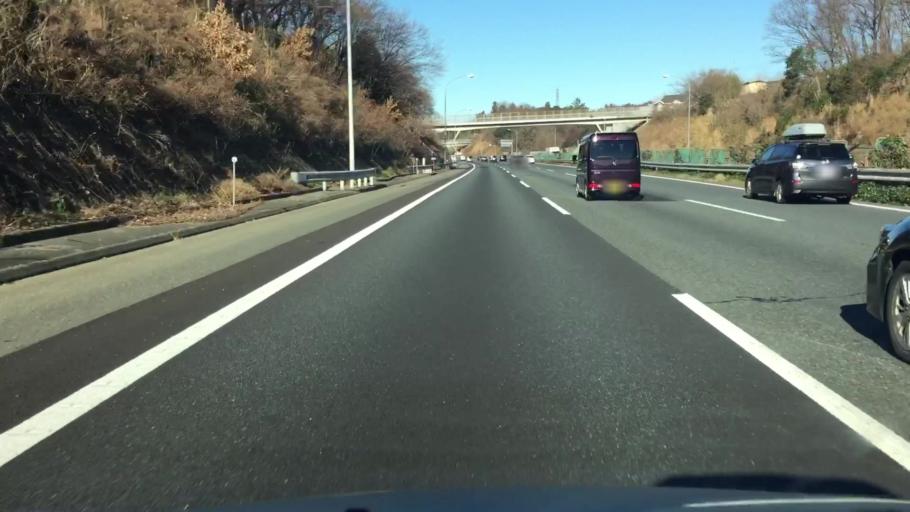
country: JP
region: Saitama
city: Ogawa
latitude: 36.0615
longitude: 139.3270
